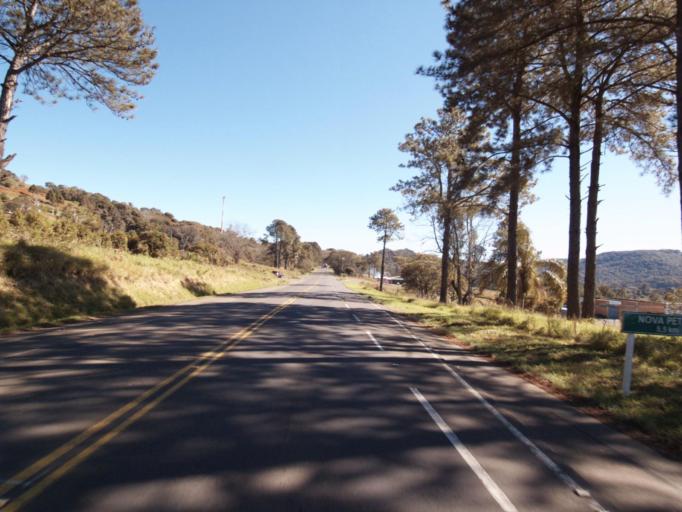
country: BR
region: Santa Catarina
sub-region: Joacaba
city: Joacaba
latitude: -27.1513
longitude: -51.6038
